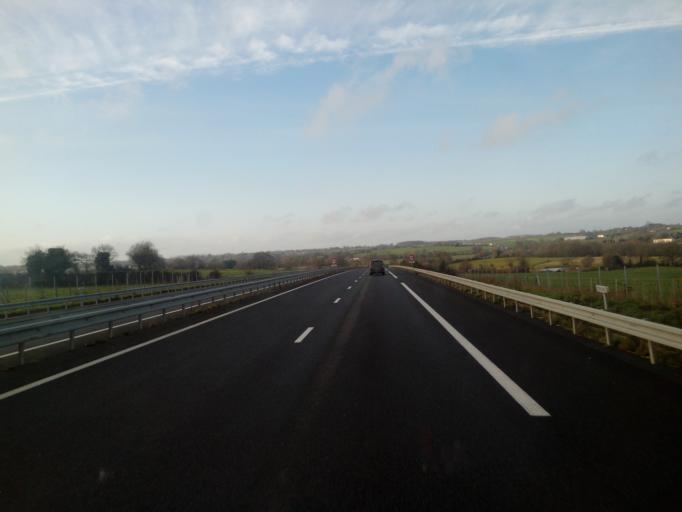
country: FR
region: Poitou-Charentes
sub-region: Departement des Deux-Sevres
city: Combrand
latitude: 46.9053
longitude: -0.6730
